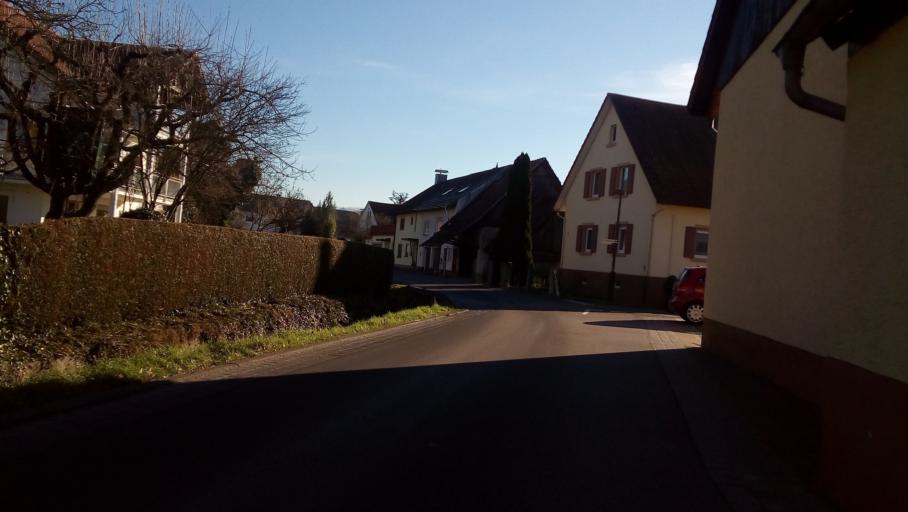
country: DE
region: Baden-Wuerttemberg
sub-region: Freiburg Region
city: Achern
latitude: 48.6551
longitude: 8.0453
